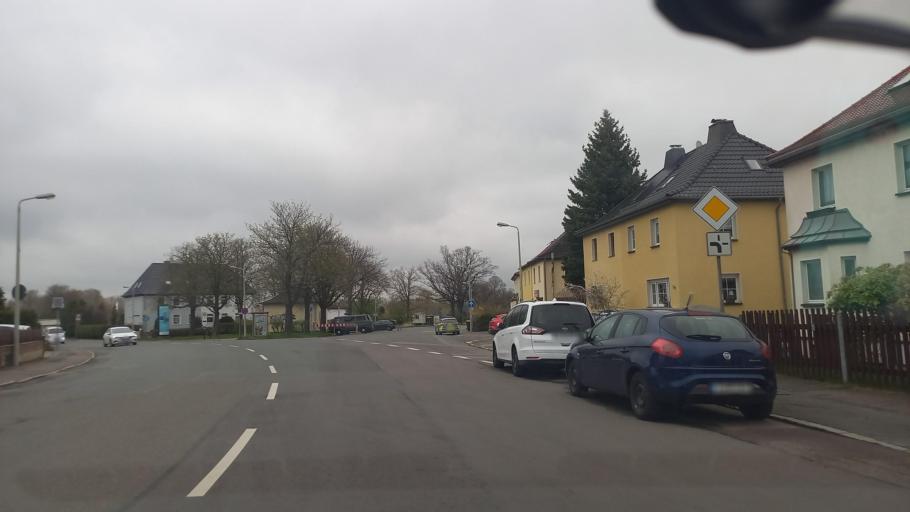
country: DE
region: Saxony
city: Zwickau
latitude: 50.7025
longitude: 12.4857
